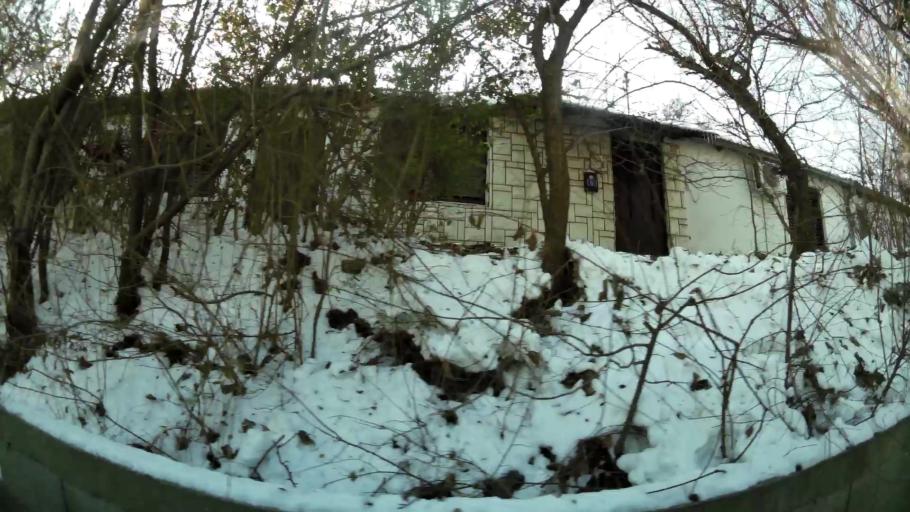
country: MK
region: Karpos
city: Skopje
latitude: 41.9878
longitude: 21.4180
